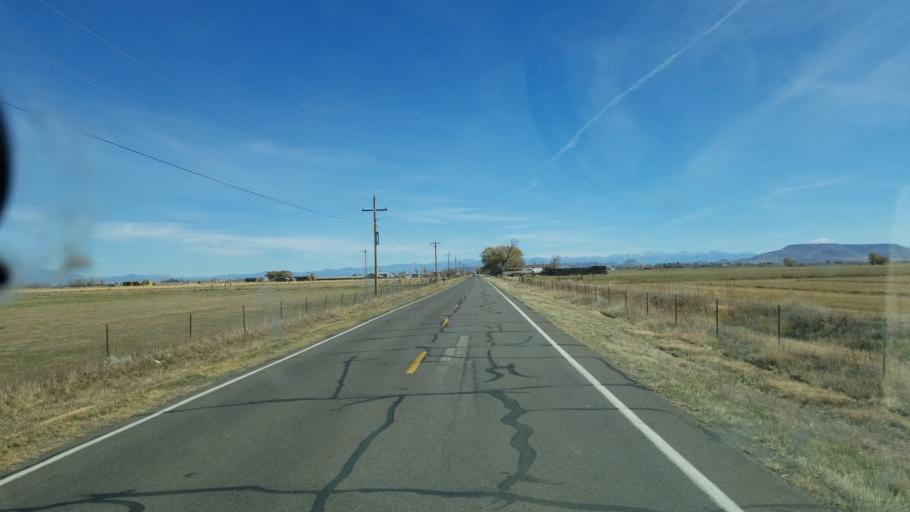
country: US
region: Colorado
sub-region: Conejos County
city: Conejos
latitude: 37.2835
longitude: -106.0033
